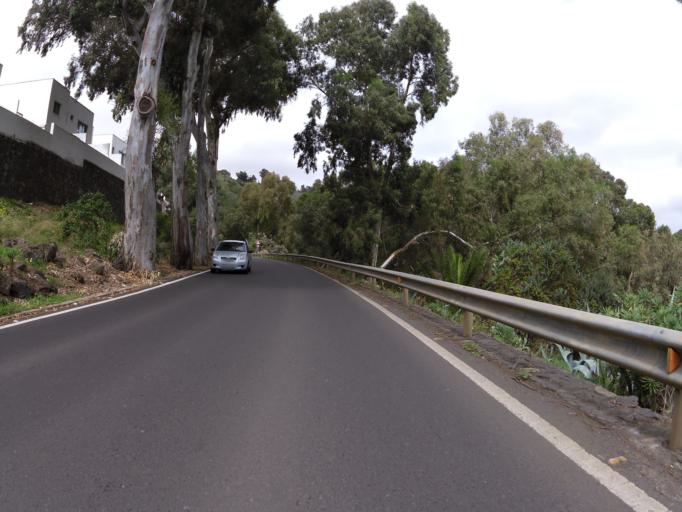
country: ES
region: Canary Islands
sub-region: Provincia de Las Palmas
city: Arucas
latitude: 28.0980
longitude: -15.5324
